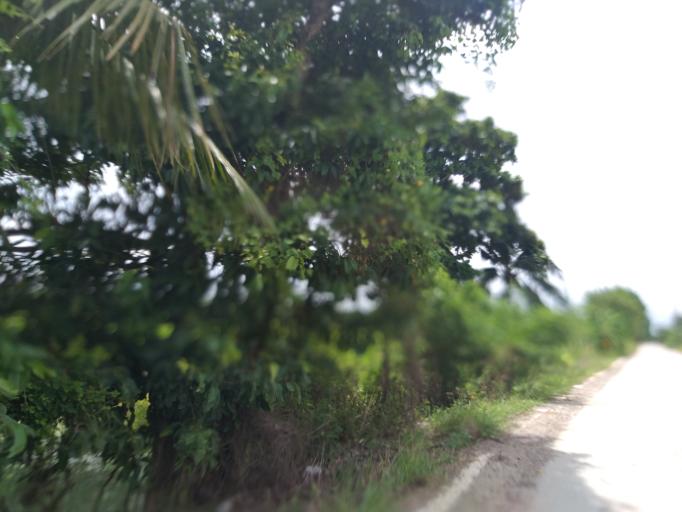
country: TH
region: Pathum Thani
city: Ban Lam Luk Ka
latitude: 14.0290
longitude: 100.8659
